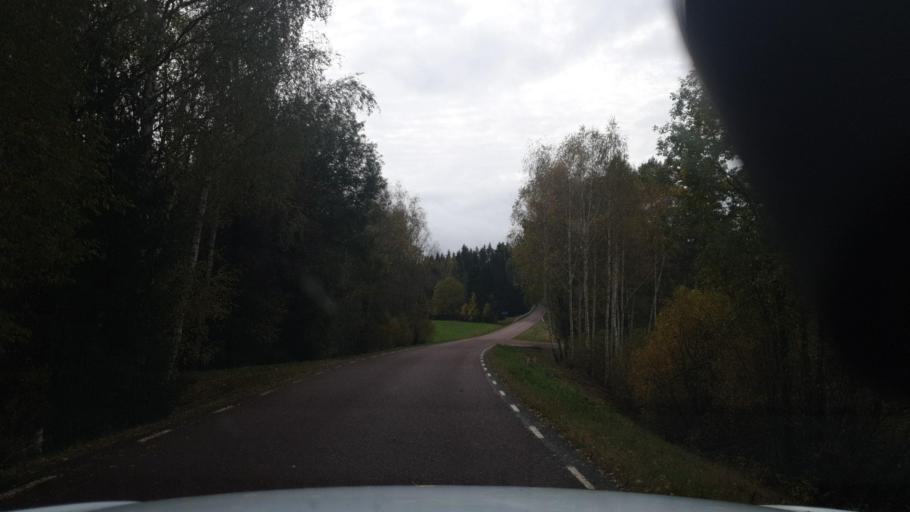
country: SE
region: Vaermland
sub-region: Karlstads Kommun
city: Edsvalla
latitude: 59.4963
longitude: 13.1055
